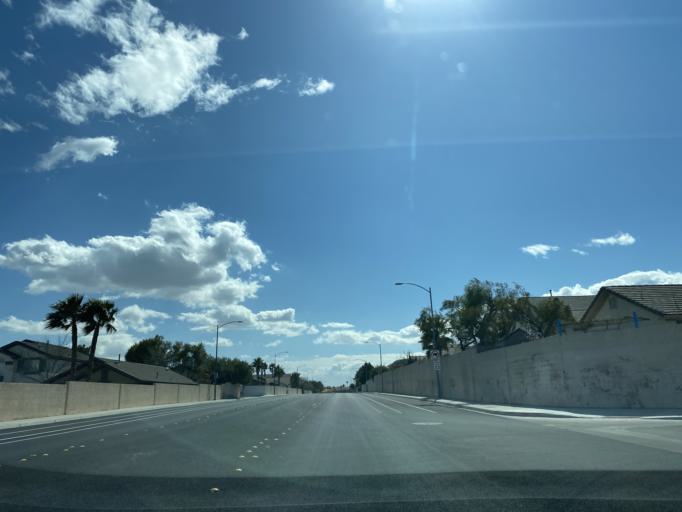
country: US
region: Nevada
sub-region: Clark County
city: Summerlin South
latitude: 36.2326
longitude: -115.3065
